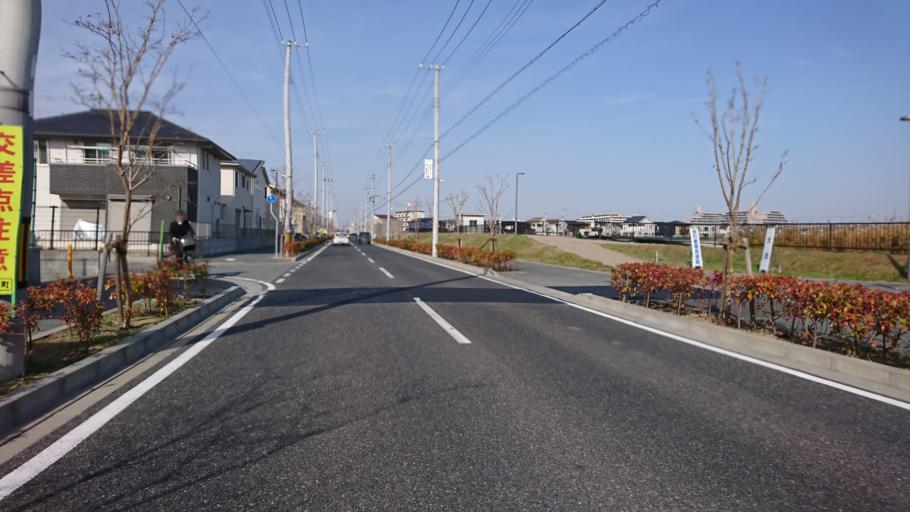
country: JP
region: Hyogo
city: Kakogawacho-honmachi
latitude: 34.7101
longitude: 134.8708
